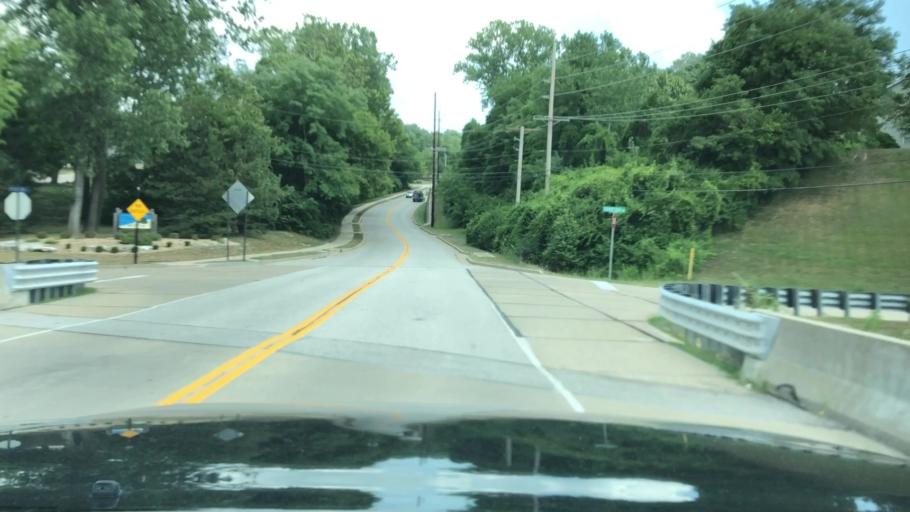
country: US
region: Missouri
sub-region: Saint Charles County
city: Saint Charles
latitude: 38.8055
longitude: -90.5514
